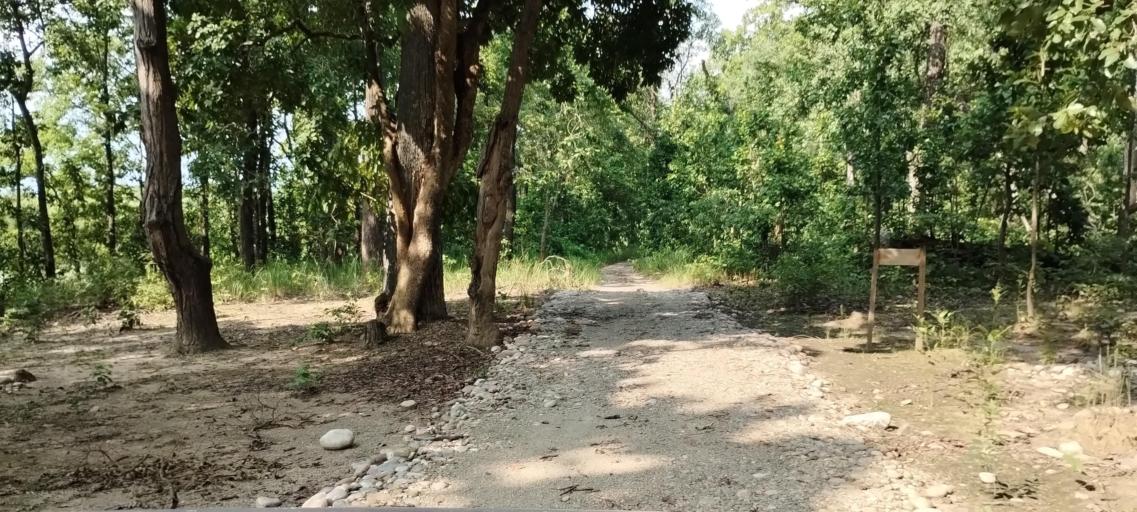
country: NP
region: Far Western
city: Tikapur
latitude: 28.5552
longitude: 81.2634
